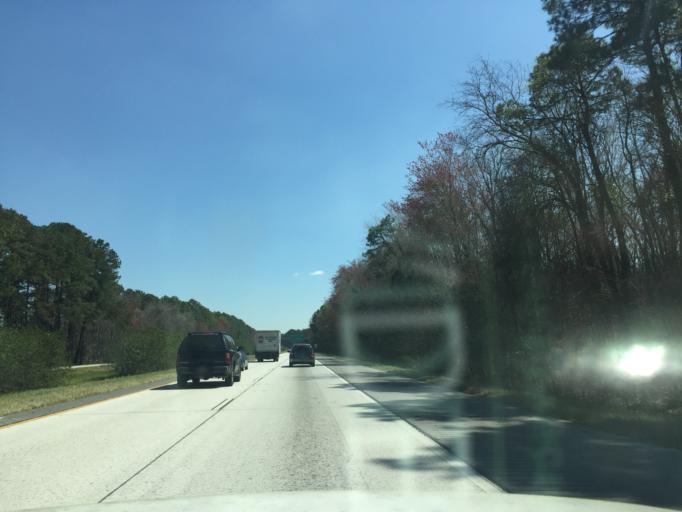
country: US
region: Georgia
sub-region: Chatham County
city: Pooler
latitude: 32.0777
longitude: -81.2626
